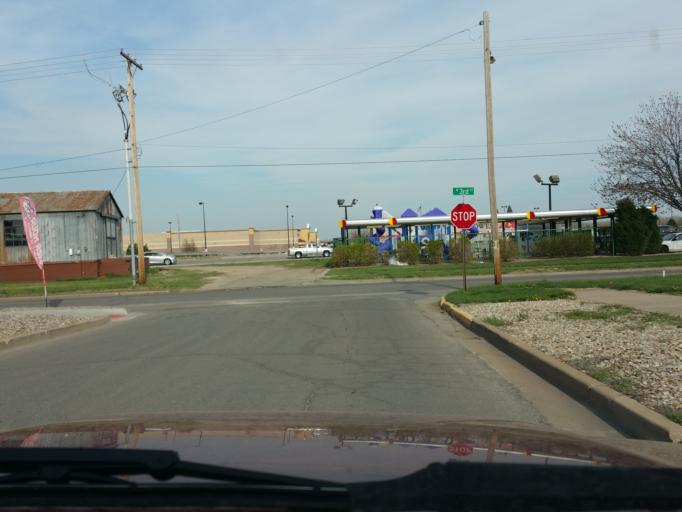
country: US
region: Kansas
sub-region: Riley County
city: Manhattan
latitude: 39.1877
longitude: -96.5604
